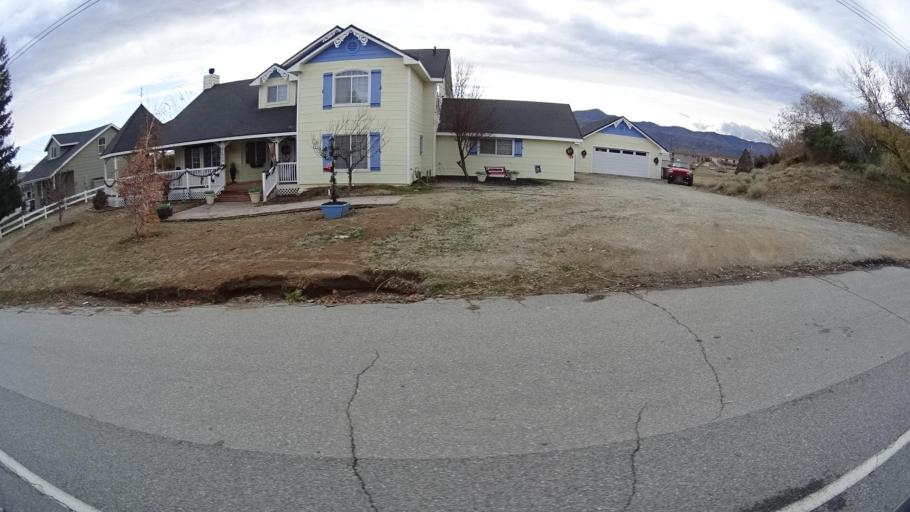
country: US
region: California
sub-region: Kern County
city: Golden Hills
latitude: 35.1523
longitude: -118.5024
